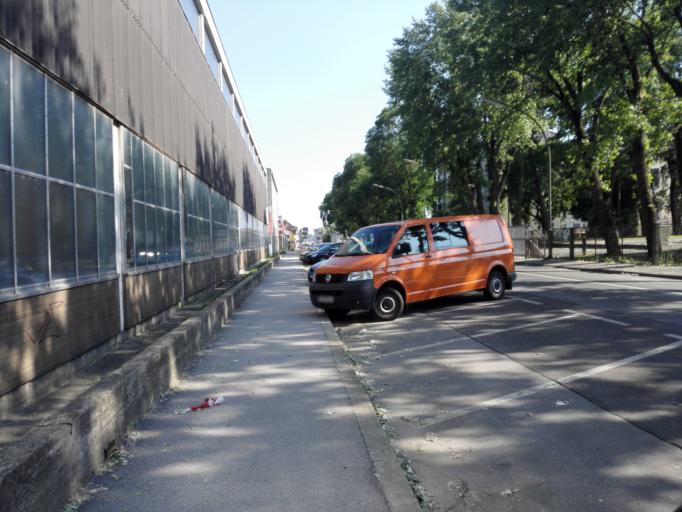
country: AT
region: Styria
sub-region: Graz Stadt
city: Wetzelsdorf
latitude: 47.0743
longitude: 15.4136
